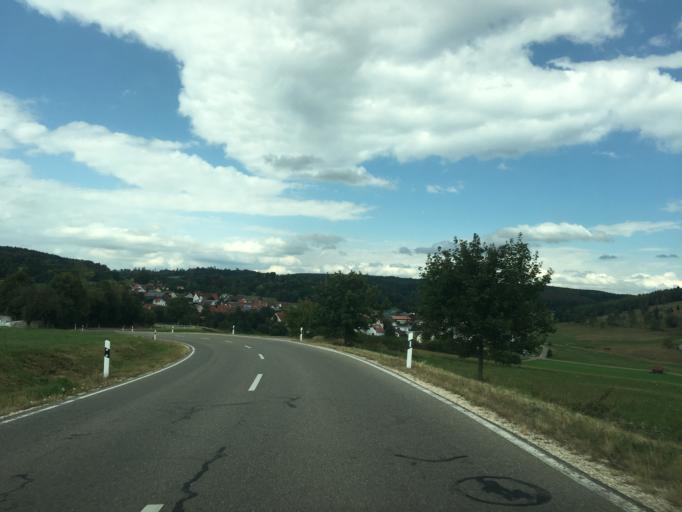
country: DE
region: Baden-Wuerttemberg
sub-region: Tuebingen Region
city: Hayingen
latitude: 48.3187
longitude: 9.4400
